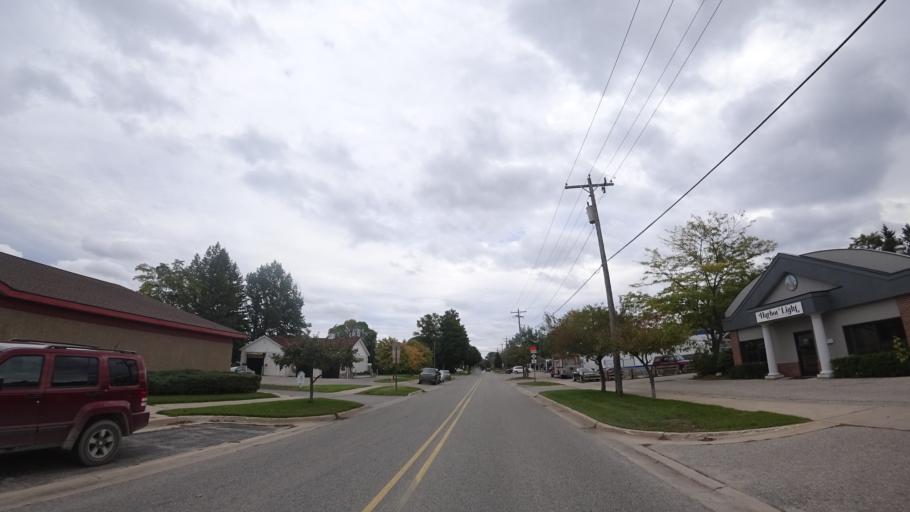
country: US
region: Michigan
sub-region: Emmet County
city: Harbor Springs
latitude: 45.4353
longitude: -84.9929
